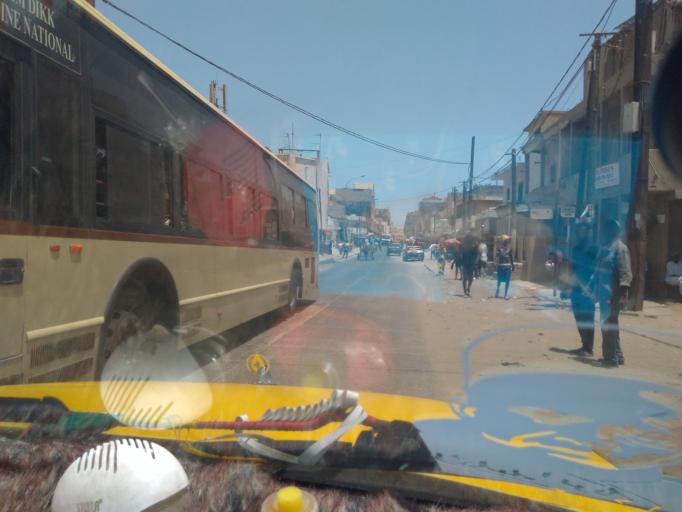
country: SN
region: Dakar
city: Grand Dakar
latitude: 14.7385
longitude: -17.4453
